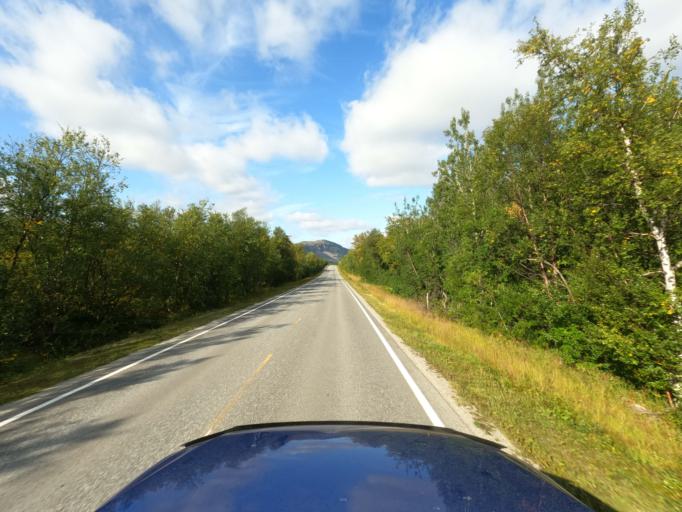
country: NO
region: Finnmark Fylke
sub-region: Porsanger
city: Lakselv
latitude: 69.9386
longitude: 24.9714
